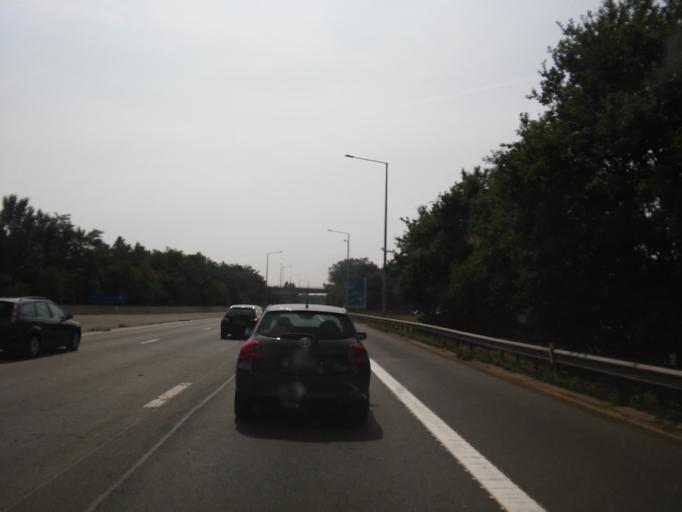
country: BE
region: Flanders
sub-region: Provincie Antwerpen
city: Rumst
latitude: 51.0548
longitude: 4.4503
